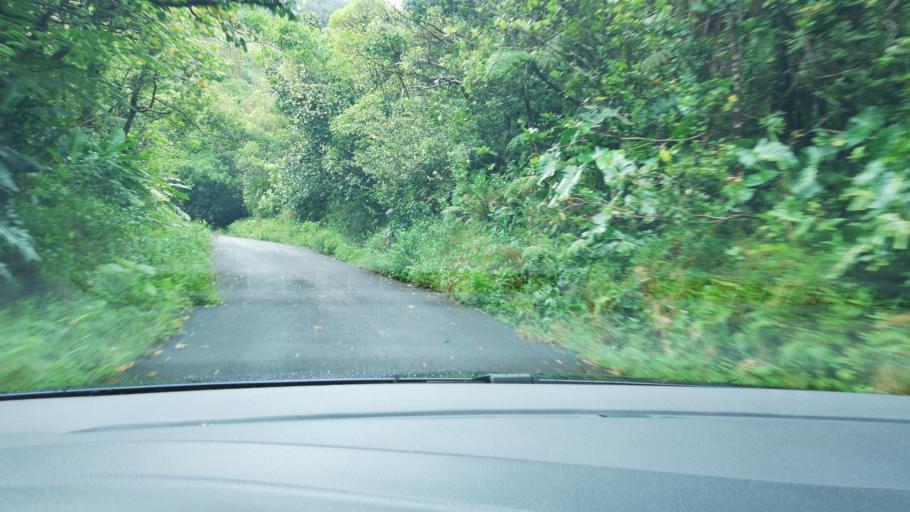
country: GP
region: Guadeloupe
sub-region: Guadeloupe
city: Saint-Claude
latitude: 16.0358
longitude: -61.6679
